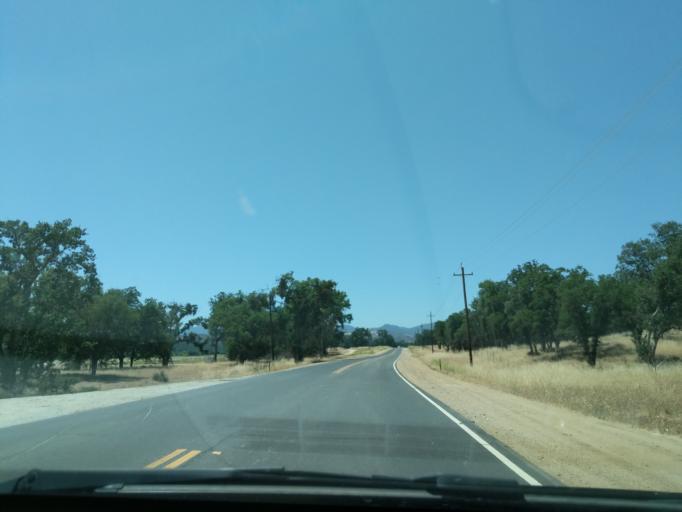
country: US
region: California
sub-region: Monterey County
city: King City
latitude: 35.9696
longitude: -121.1958
